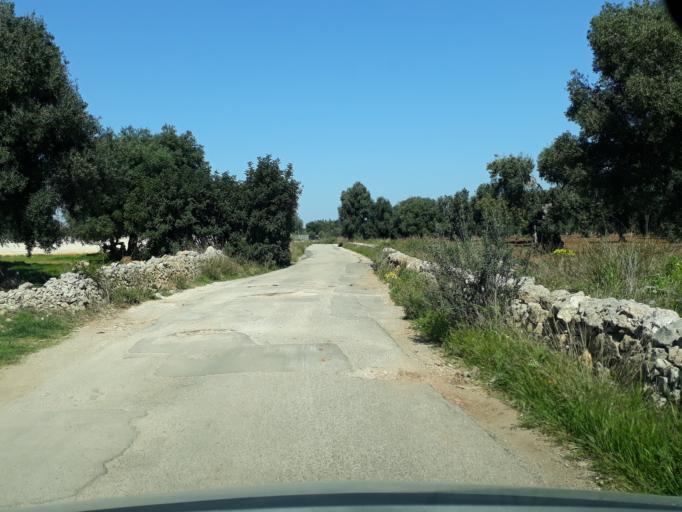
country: IT
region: Apulia
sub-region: Provincia di Brindisi
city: Fasano
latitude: 40.8278
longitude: 17.3820
